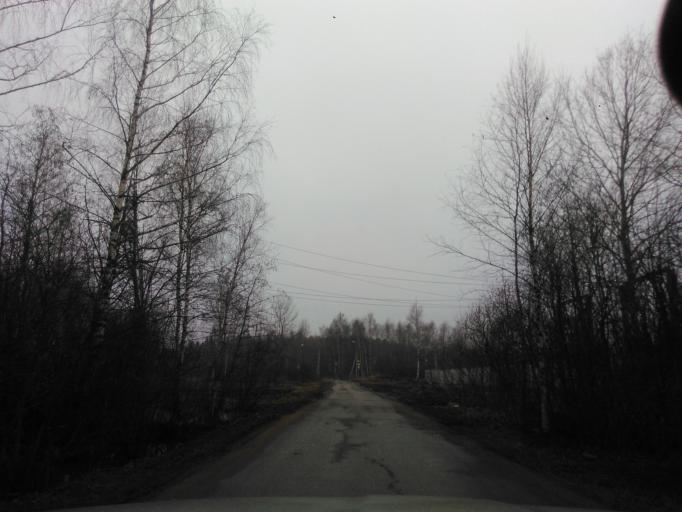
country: RU
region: Moskovskaya
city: Andreyevka
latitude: 55.9284
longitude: 37.1513
